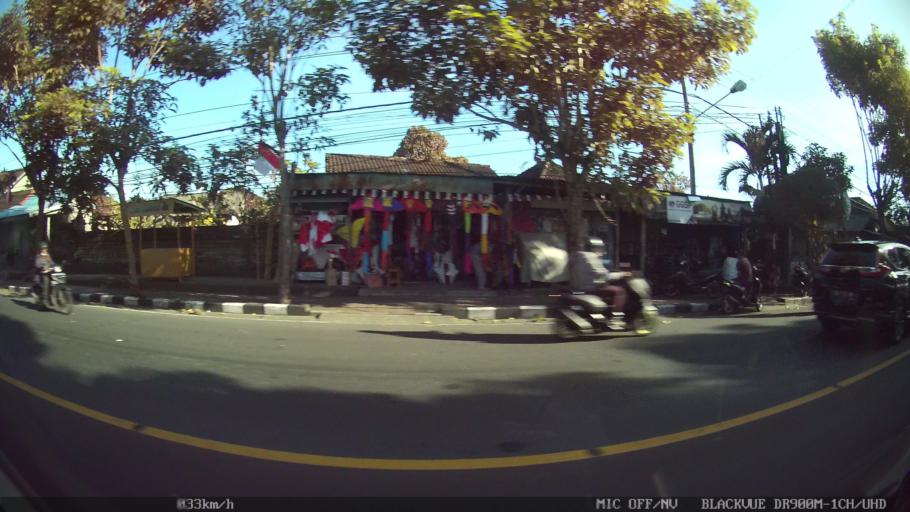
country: ID
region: Bali
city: Banjar Karangsuling
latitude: -8.6086
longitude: 115.1894
